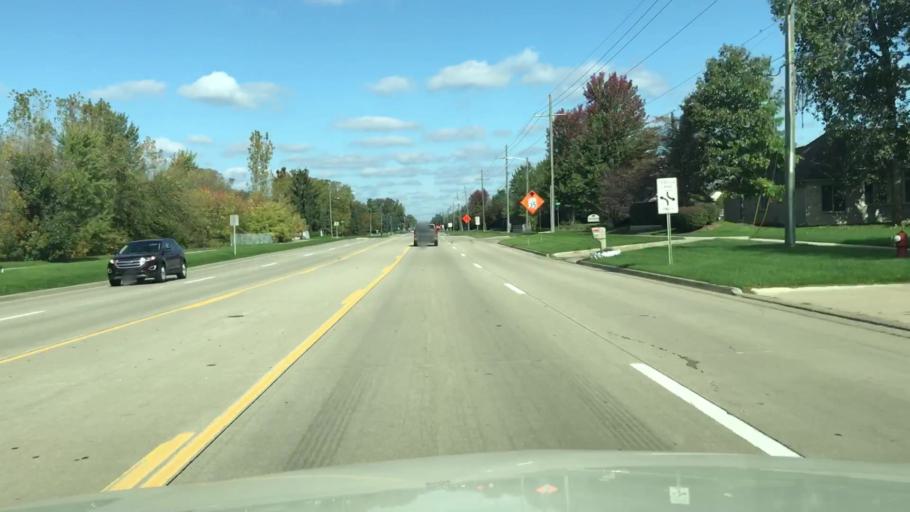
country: US
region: Michigan
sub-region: Macomb County
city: Sterling Heights
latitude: 42.5856
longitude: -83.0896
